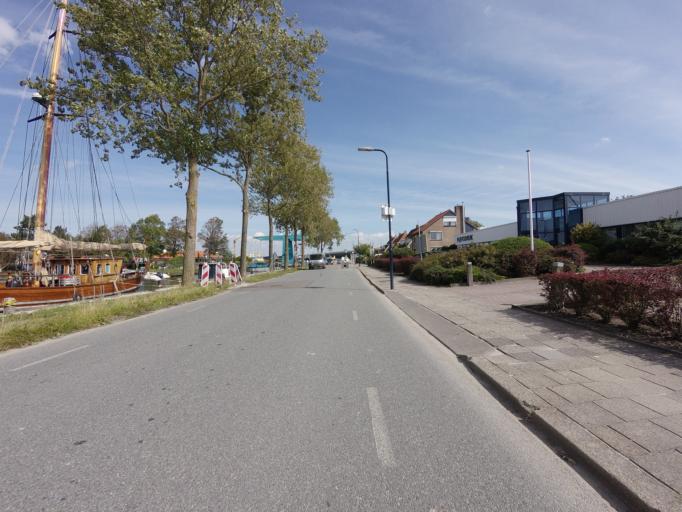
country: NL
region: Friesland
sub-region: Gemeente Harlingen
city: Harlingen
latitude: 53.1743
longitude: 5.4350
